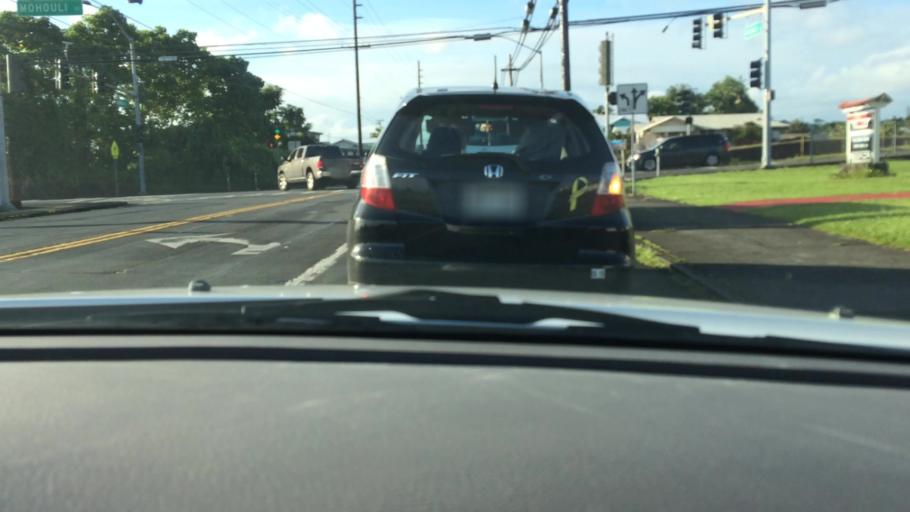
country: US
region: Hawaii
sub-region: Hawaii County
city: Hilo
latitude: 19.7121
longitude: -155.0808
